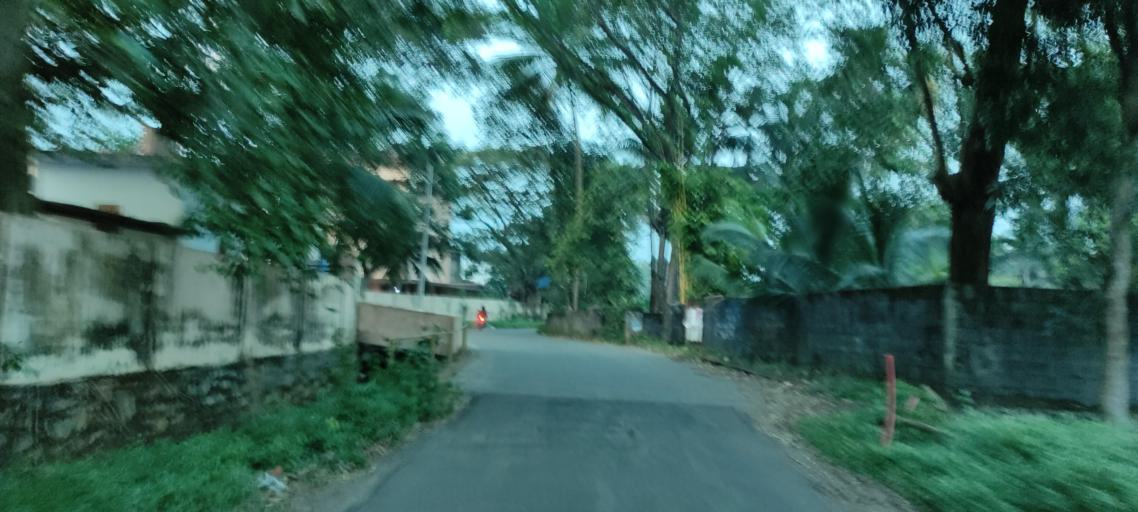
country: IN
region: Kerala
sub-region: Pattanamtitta
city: Adur
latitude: 9.1586
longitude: 76.7385
